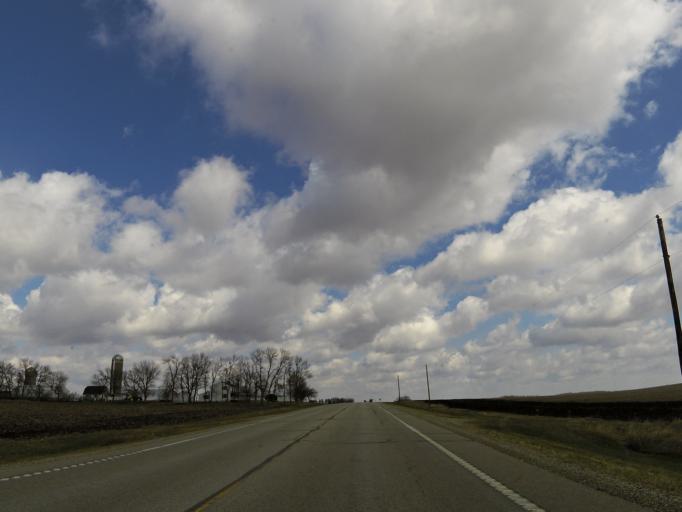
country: US
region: Minnesota
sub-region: Dodge County
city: Mantorville
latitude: 44.0803
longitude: -92.8044
